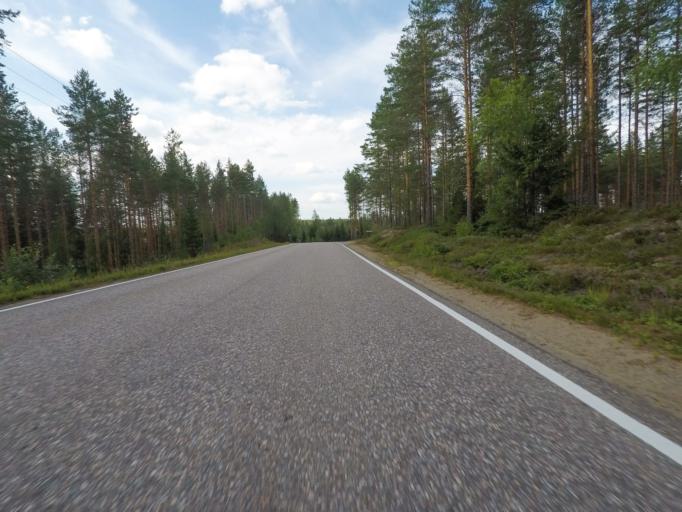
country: FI
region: Southern Savonia
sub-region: Savonlinna
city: Sulkava
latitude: 61.7402
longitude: 28.1981
